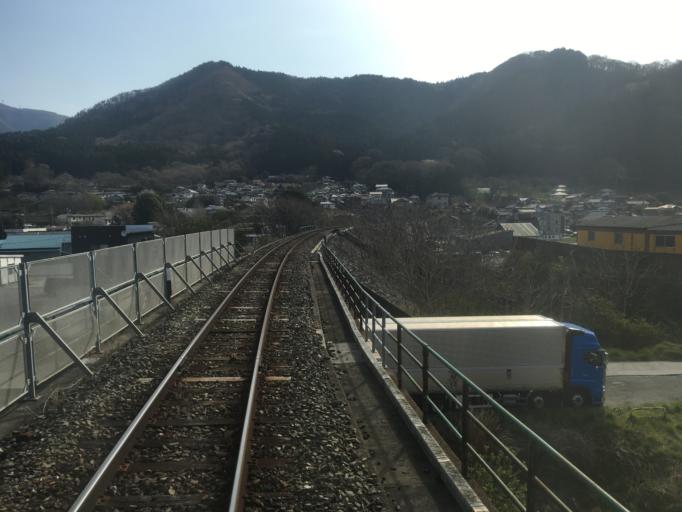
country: JP
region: Iwate
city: Ofunato
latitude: 39.0804
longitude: 141.7211
